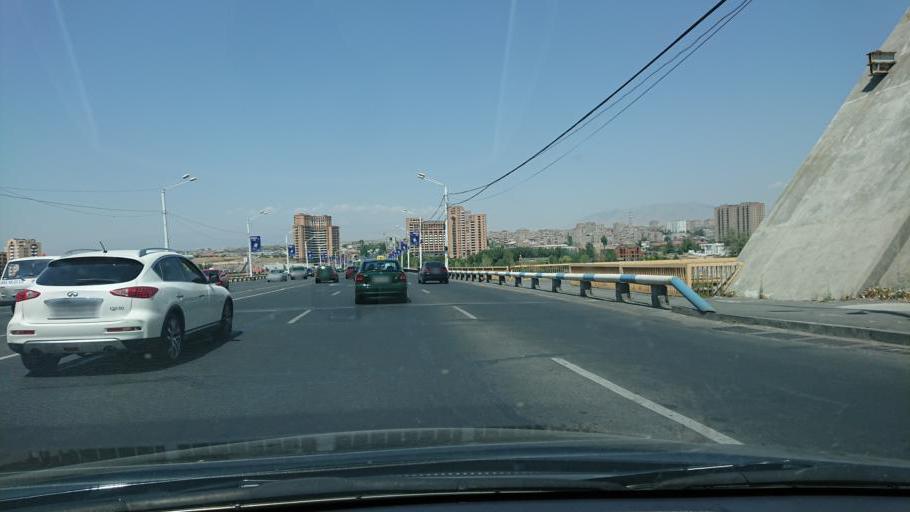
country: AM
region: Yerevan
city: Yerevan
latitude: 40.2077
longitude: 44.4951
